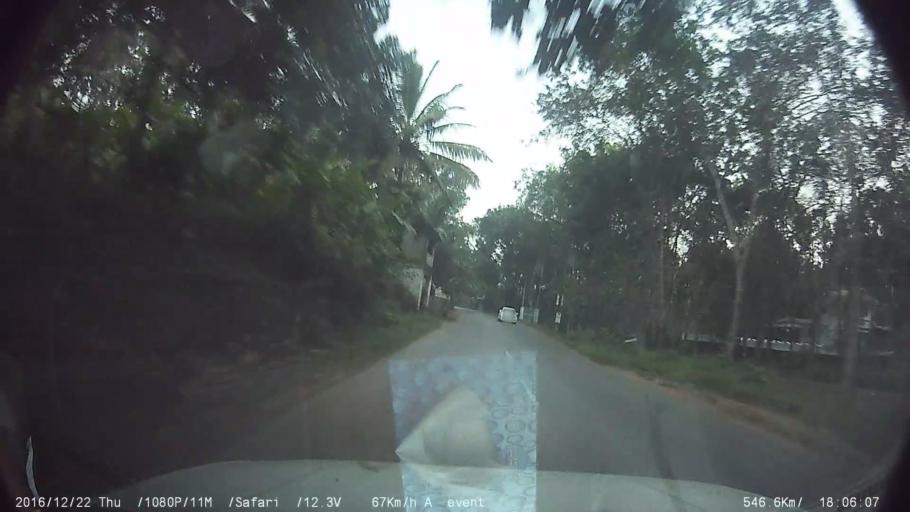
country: IN
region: Kerala
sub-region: Kottayam
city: Palackattumala
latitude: 9.8223
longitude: 76.6082
